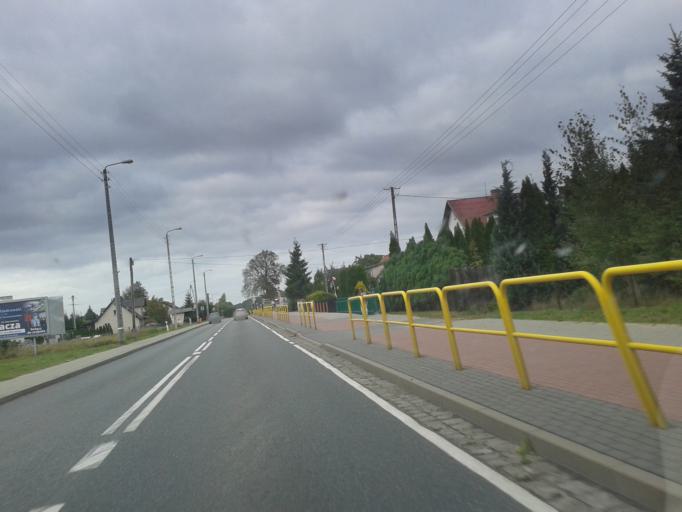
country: PL
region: Kujawsko-Pomorskie
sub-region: Powiat sepolenski
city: Sepolno Krajenskie
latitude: 53.4634
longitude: 17.5304
